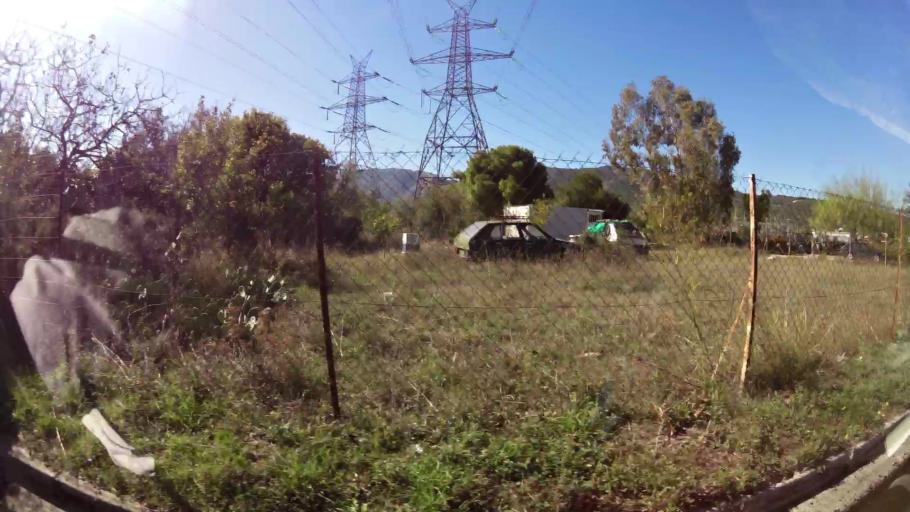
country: GR
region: Attica
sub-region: Nomarchia Anatolikis Attikis
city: Leondarion
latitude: 37.9949
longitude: 23.8589
